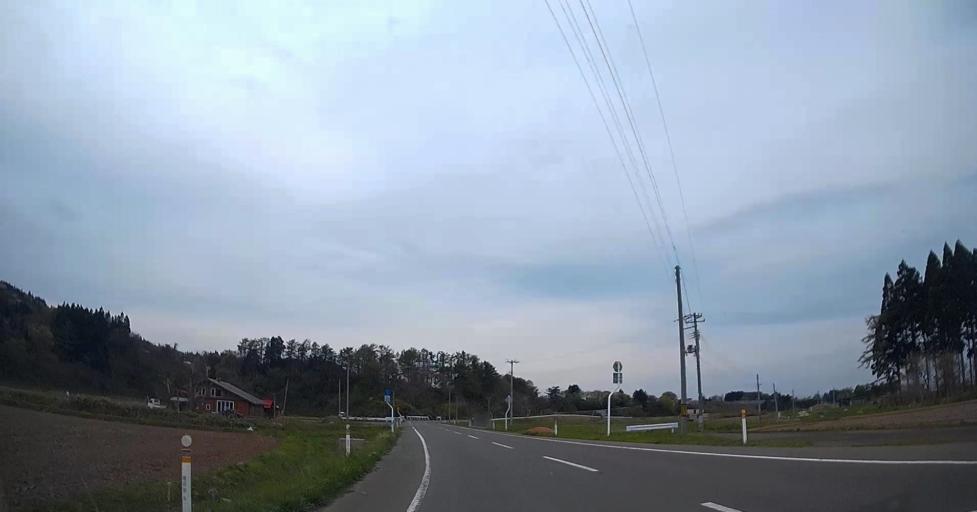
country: JP
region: Aomori
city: Goshogawara
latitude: 40.9016
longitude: 140.4933
